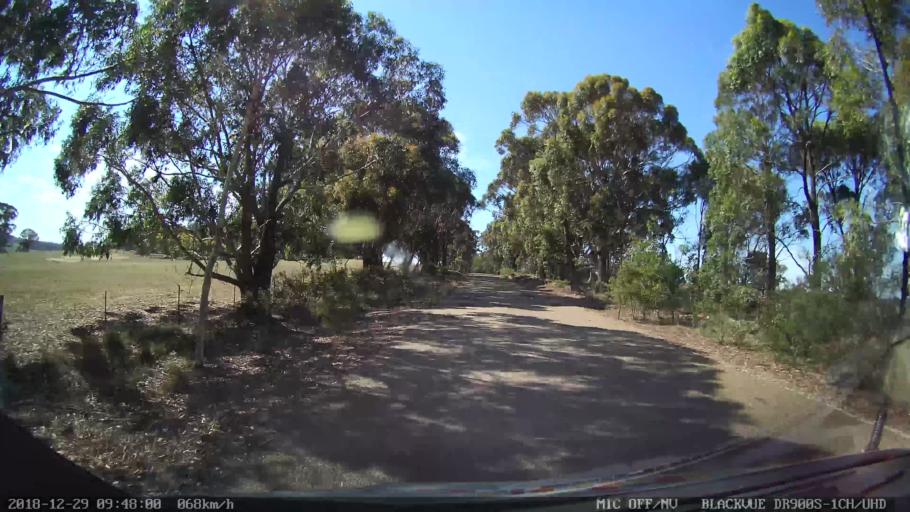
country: AU
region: New South Wales
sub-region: Upper Lachlan Shire
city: Crookwell
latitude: -34.7120
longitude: 149.4533
